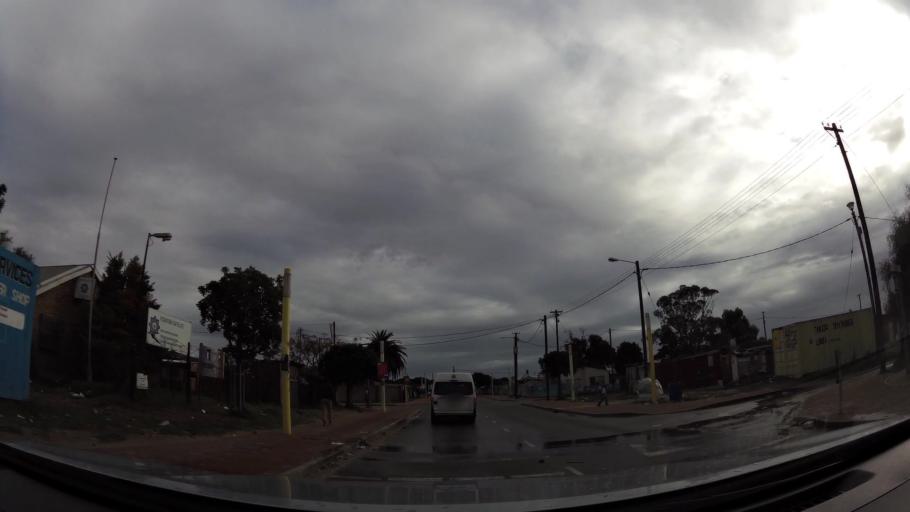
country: ZA
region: Eastern Cape
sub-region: Nelson Mandela Bay Metropolitan Municipality
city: Port Elizabeth
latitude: -33.9874
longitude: 25.5891
